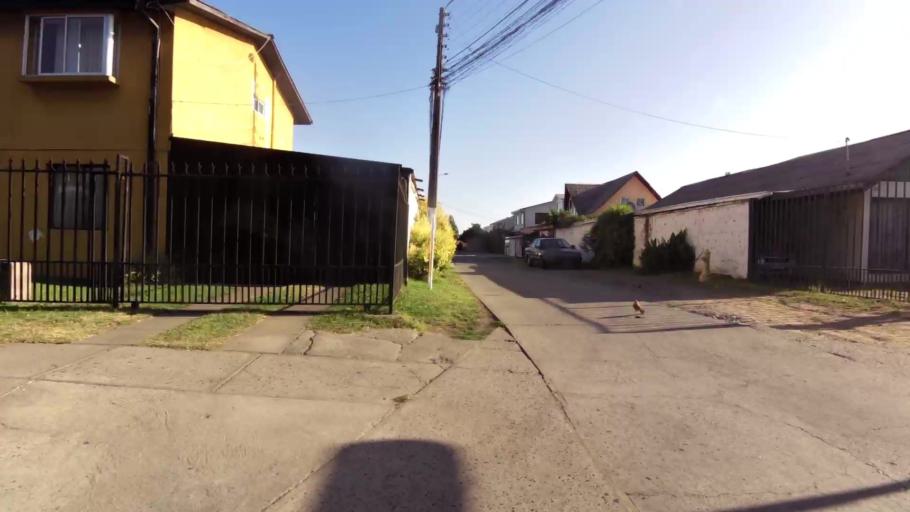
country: CL
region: Maule
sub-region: Provincia de Talca
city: Talca
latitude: -35.4359
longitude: -71.6570
